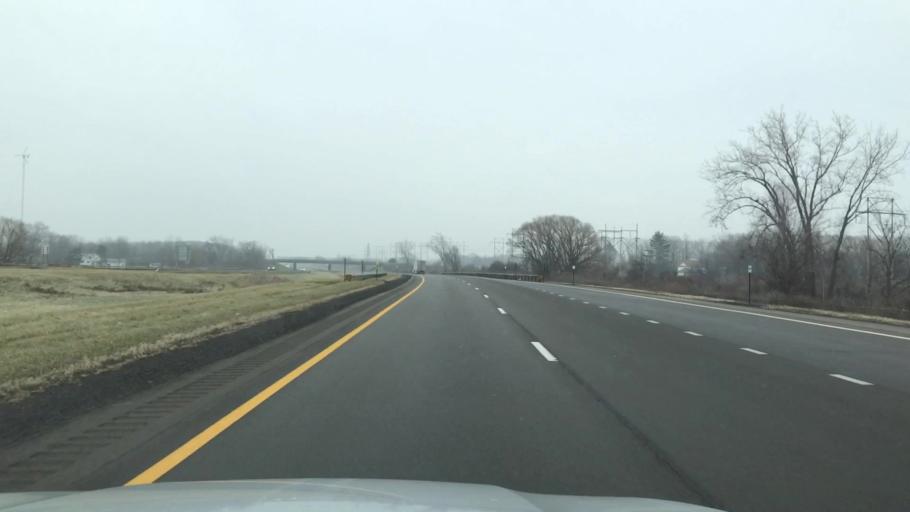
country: US
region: New York
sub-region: Chautauqua County
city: Dunkirk
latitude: 42.4628
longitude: -79.2999
